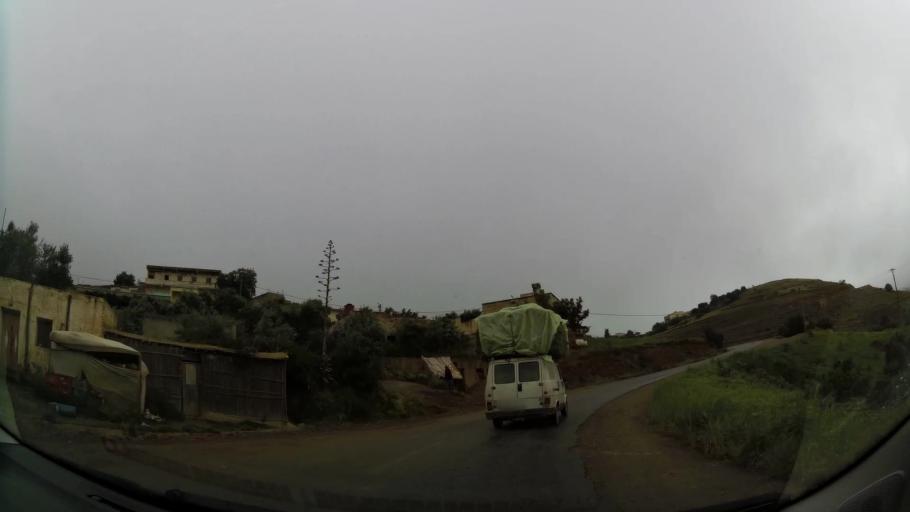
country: MA
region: Oriental
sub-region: Nador
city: Boudinar
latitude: 35.0901
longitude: -3.5240
